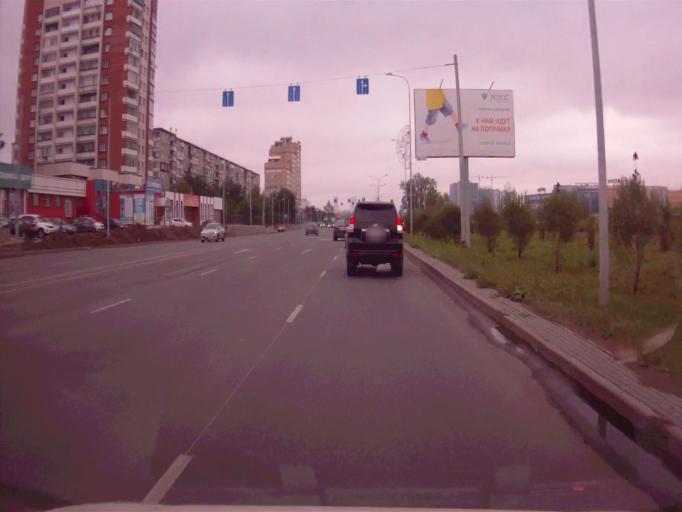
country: RU
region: Chelyabinsk
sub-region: Gorod Chelyabinsk
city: Chelyabinsk
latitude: 55.1736
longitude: 61.3490
